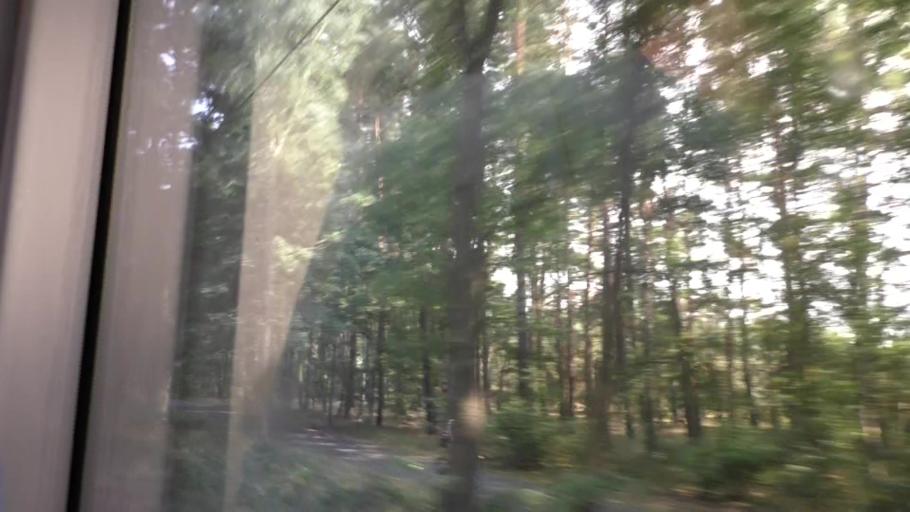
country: DE
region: Brandenburg
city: Bestensee
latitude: 52.2982
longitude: 13.7408
